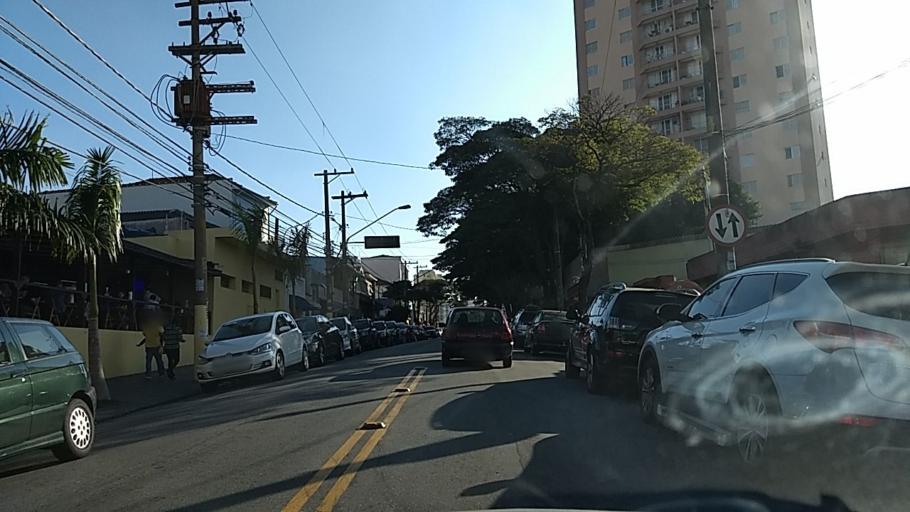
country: BR
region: Sao Paulo
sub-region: Sao Paulo
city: Sao Paulo
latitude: -23.4875
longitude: -46.6124
